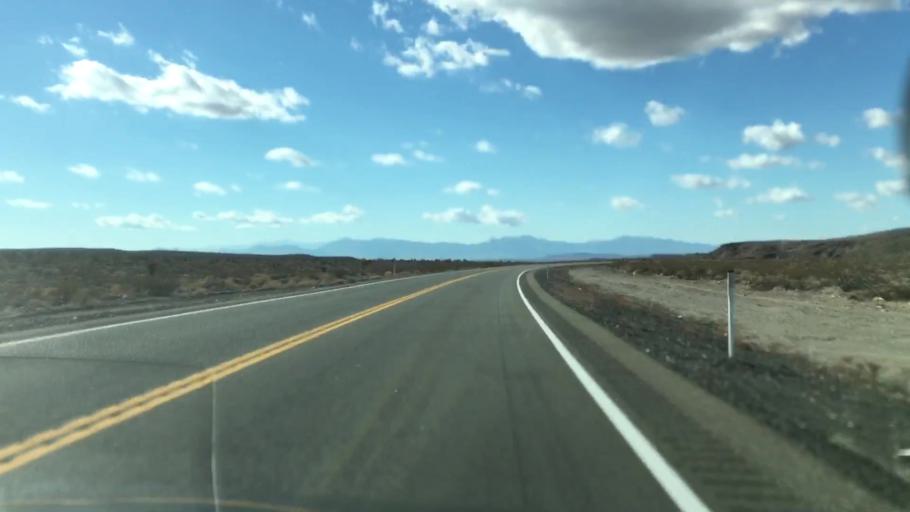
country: US
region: Nevada
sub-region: Nye County
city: Pahrump
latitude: 36.5616
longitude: -116.0926
